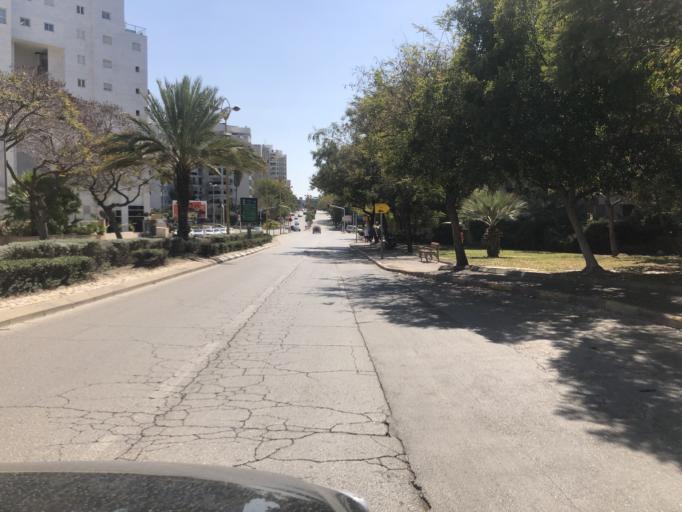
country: IL
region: Tel Aviv
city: Holon
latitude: 32.0023
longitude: 34.7677
